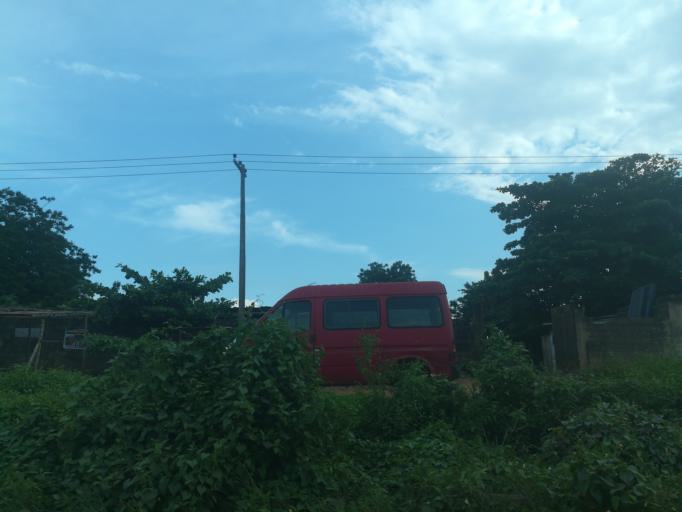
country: NG
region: Lagos
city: Ikorodu
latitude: 6.6259
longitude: 3.4995
